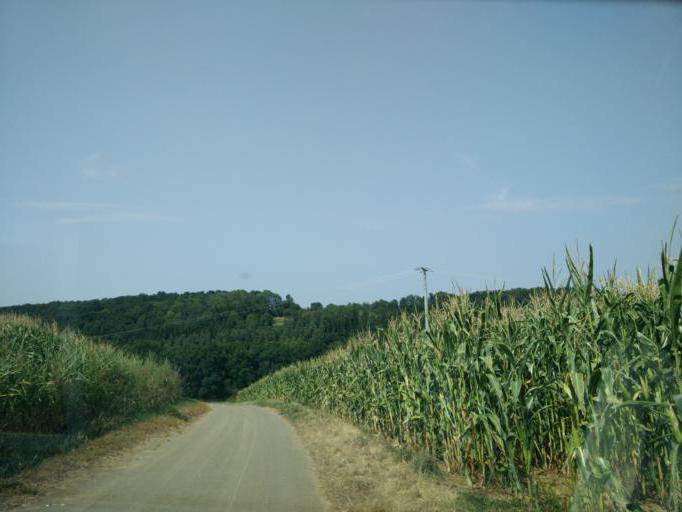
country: DE
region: Baden-Wuerttemberg
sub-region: Tuebingen Region
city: Gomaringen
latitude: 48.4734
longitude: 9.0907
